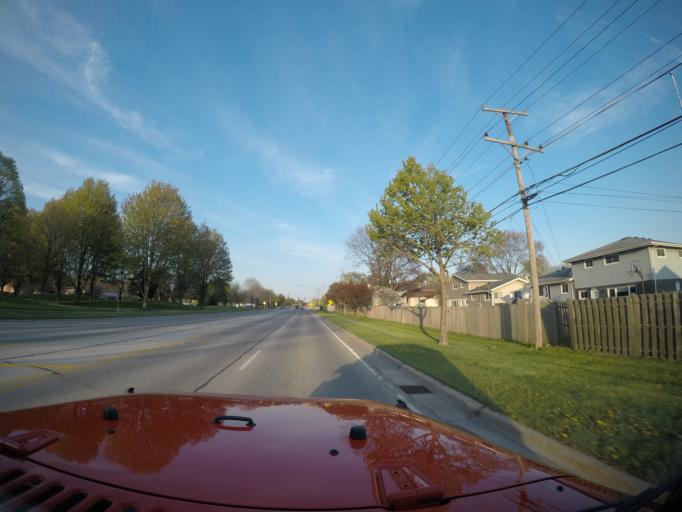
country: US
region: Illinois
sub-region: Cook County
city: Prospect Heights
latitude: 42.0878
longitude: -87.9147
